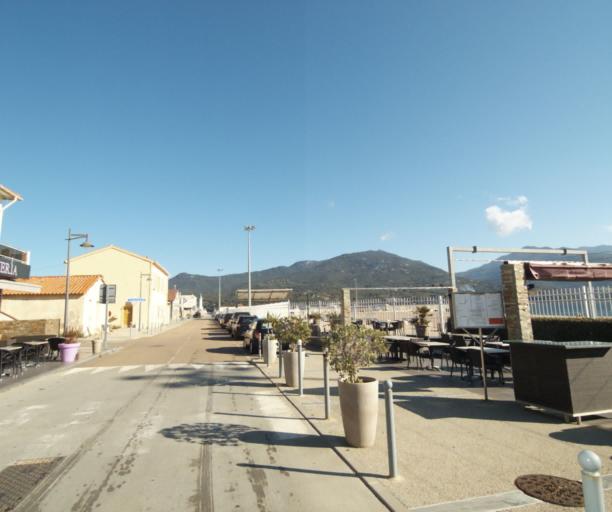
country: FR
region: Corsica
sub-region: Departement de la Corse-du-Sud
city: Propriano
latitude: 41.6760
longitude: 8.8982
